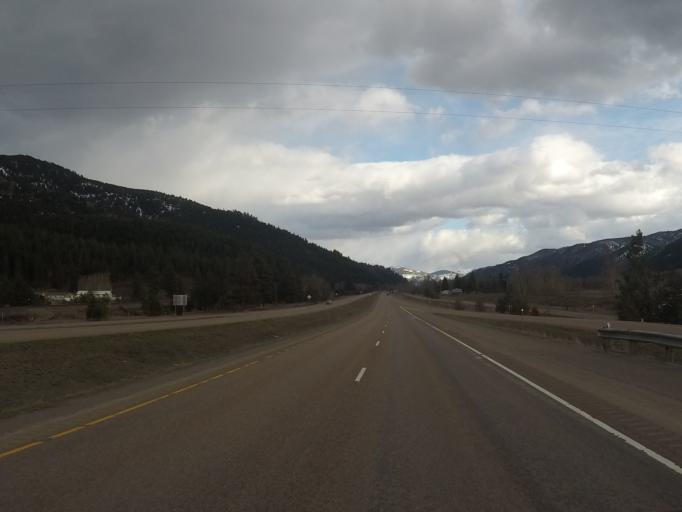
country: US
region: Montana
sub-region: Missoula County
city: Bonner-West Riverside
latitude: 46.8350
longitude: -113.8283
